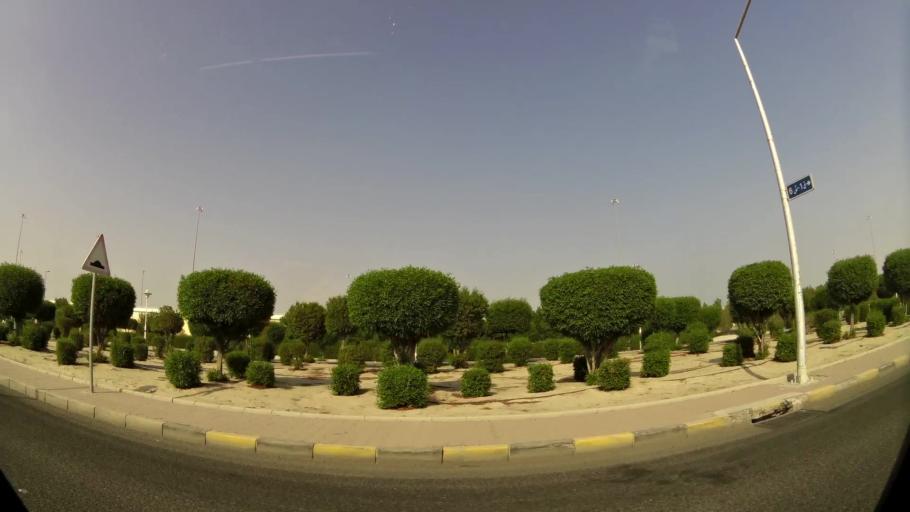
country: KW
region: Muhafazat al Jahra'
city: Al Jahra'
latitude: 29.3508
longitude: 47.6885
